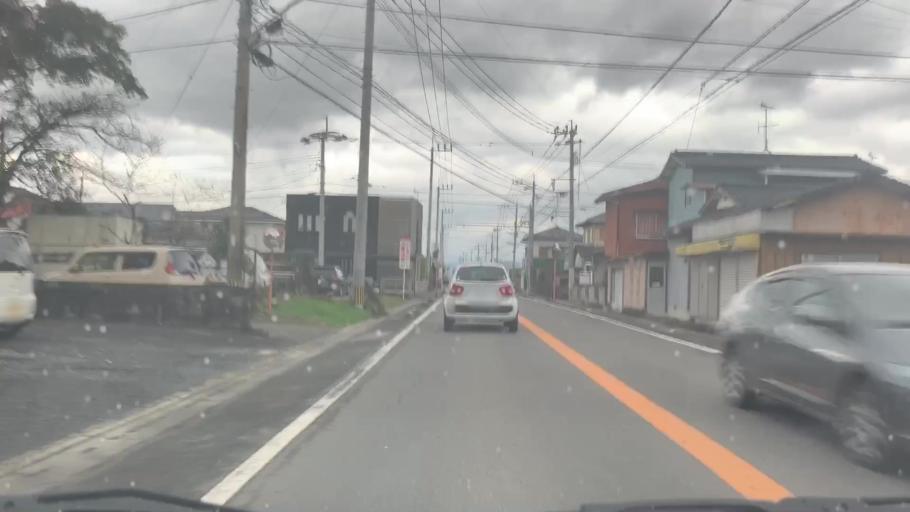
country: JP
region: Saga Prefecture
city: Saga-shi
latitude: 33.2466
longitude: 130.2657
